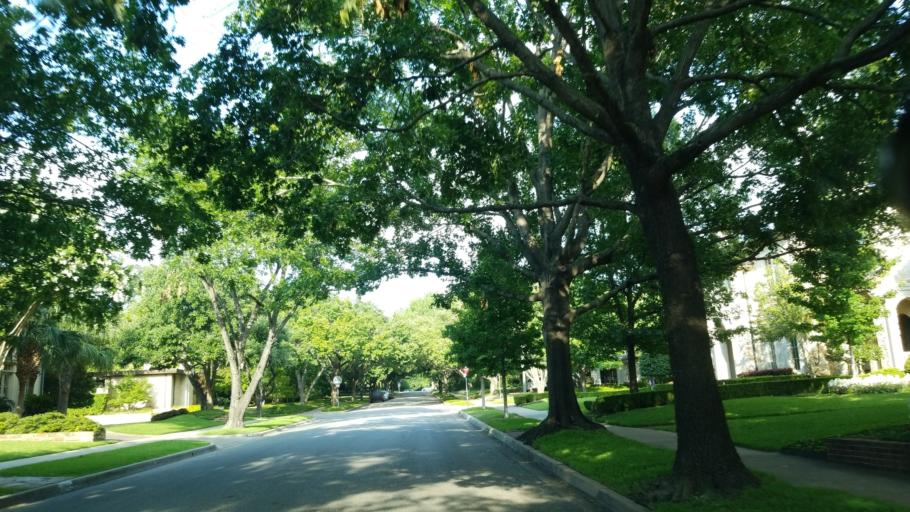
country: US
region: Texas
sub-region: Dallas County
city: Highland Park
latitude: 32.8345
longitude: -96.7897
